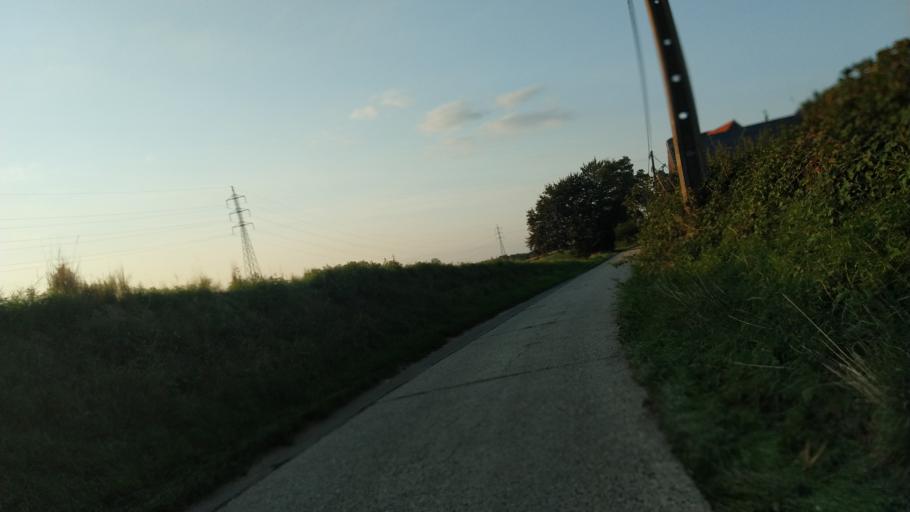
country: BE
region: Flanders
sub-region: Provincie Vlaams-Brabant
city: Lubbeek
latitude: 50.8787
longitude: 4.8045
